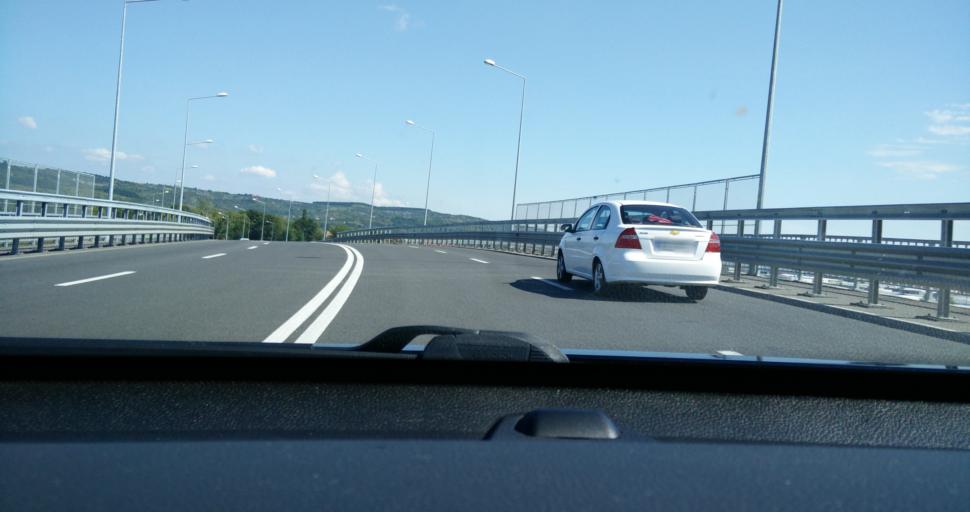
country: RO
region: Bihor
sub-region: Comuna Sanmartin
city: Sanmartin
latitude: 47.0335
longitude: 21.9957
